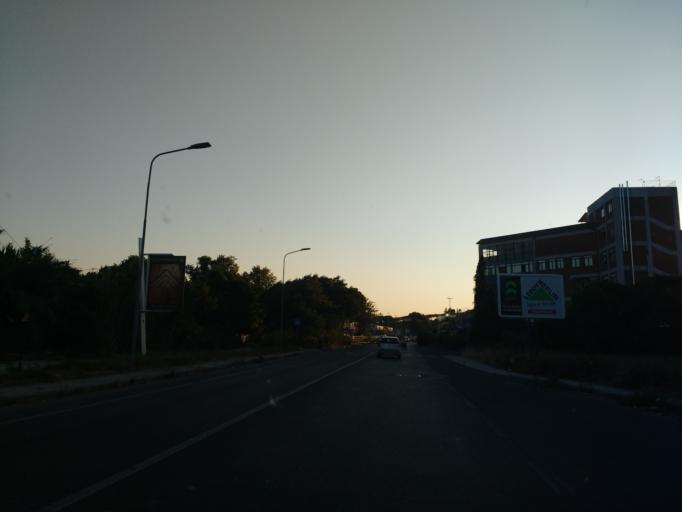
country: IT
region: Latium
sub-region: Citta metropolitana di Roma Capitale
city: Albuccione
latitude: 41.9521
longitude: 12.6937
